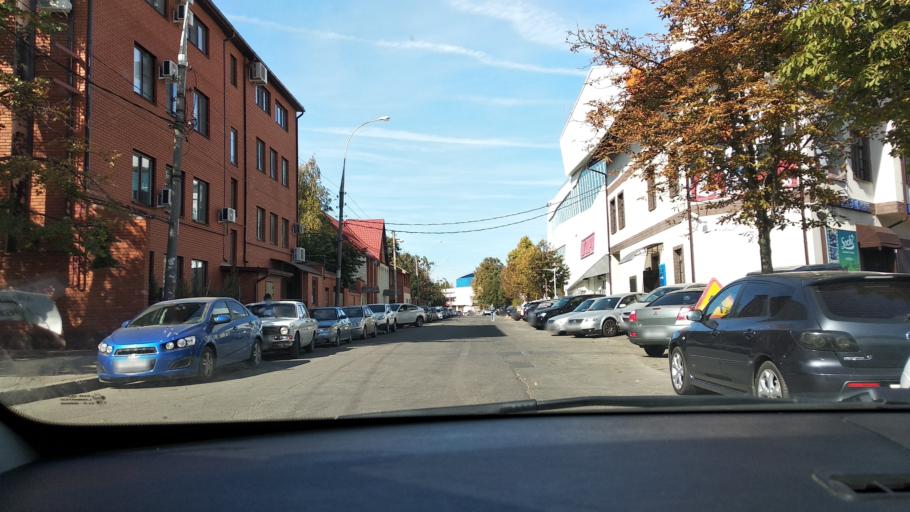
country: RU
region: Adygeya
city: Yablonovskiy
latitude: 45.0142
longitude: 38.9580
